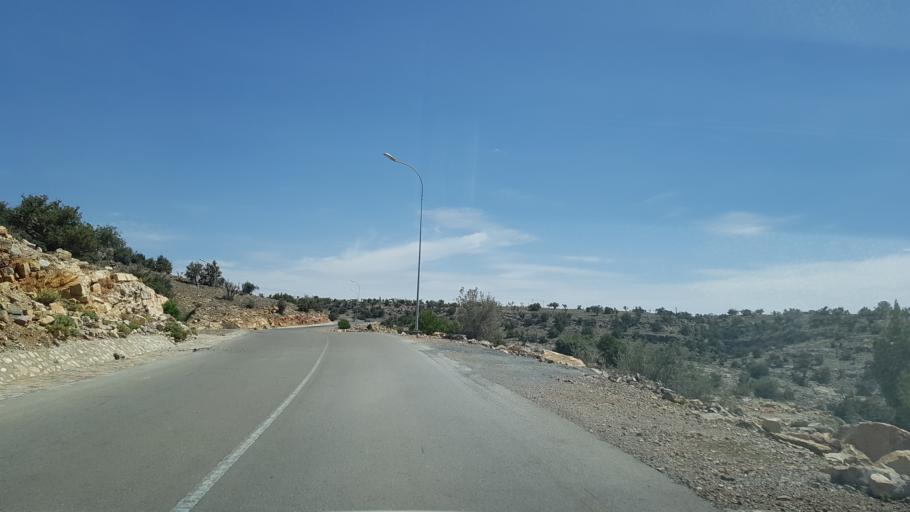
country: OM
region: Al Batinah
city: Bayt al `Awabi
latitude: 23.1392
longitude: 57.5943
